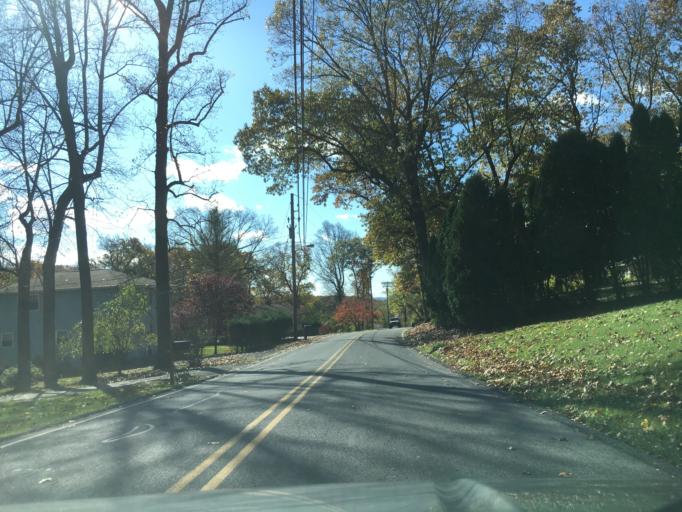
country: US
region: Pennsylvania
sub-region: Berks County
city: South Temple
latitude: 40.3969
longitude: -75.8941
